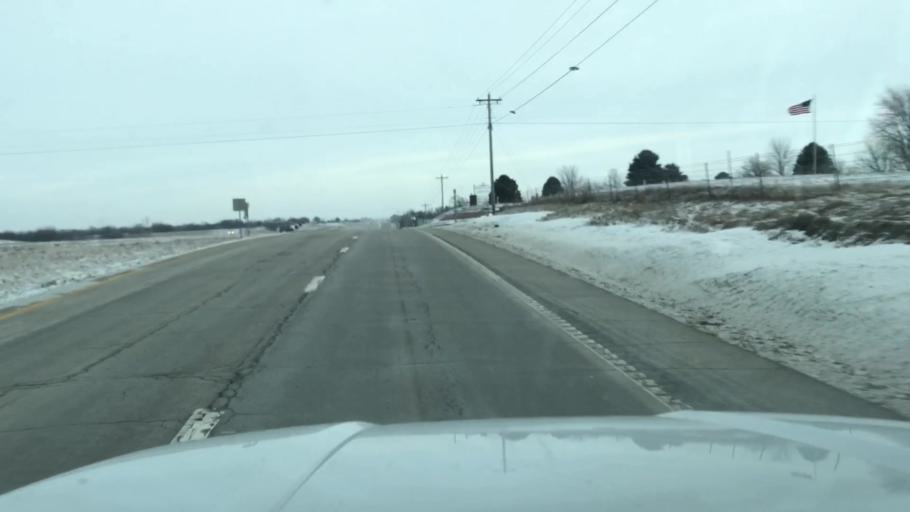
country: US
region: Missouri
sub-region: Andrew County
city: Savannah
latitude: 39.9951
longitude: -94.8798
